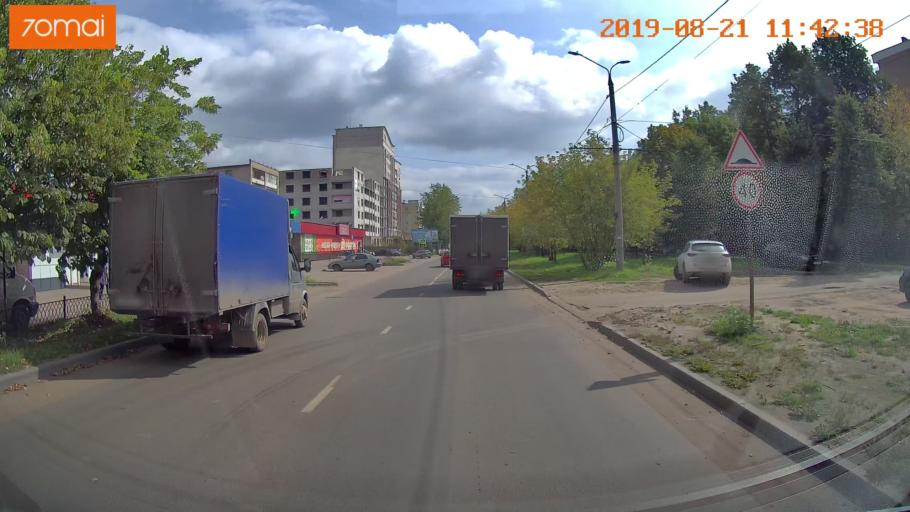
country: RU
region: Ivanovo
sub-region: Gorod Ivanovo
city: Ivanovo
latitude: 57.0018
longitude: 40.9517
